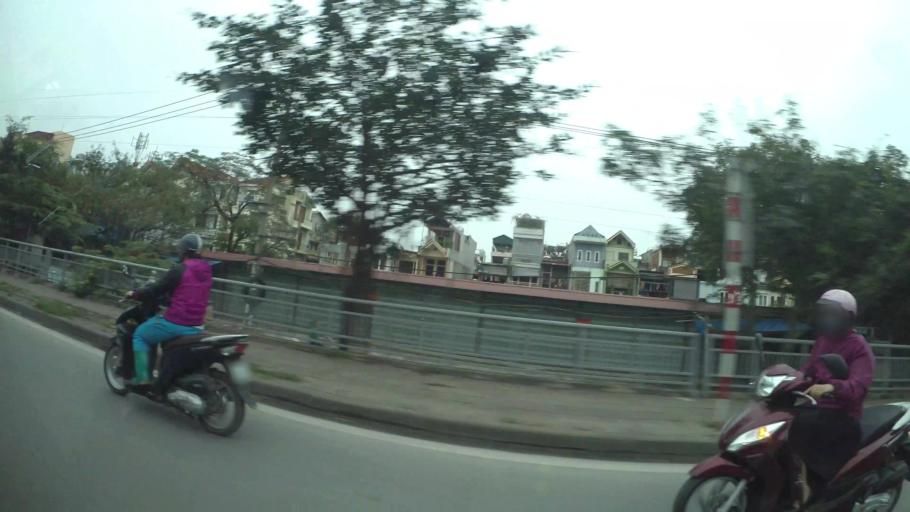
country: VN
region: Ha Noi
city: Hai BaTrung
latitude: 21.0165
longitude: 105.8626
